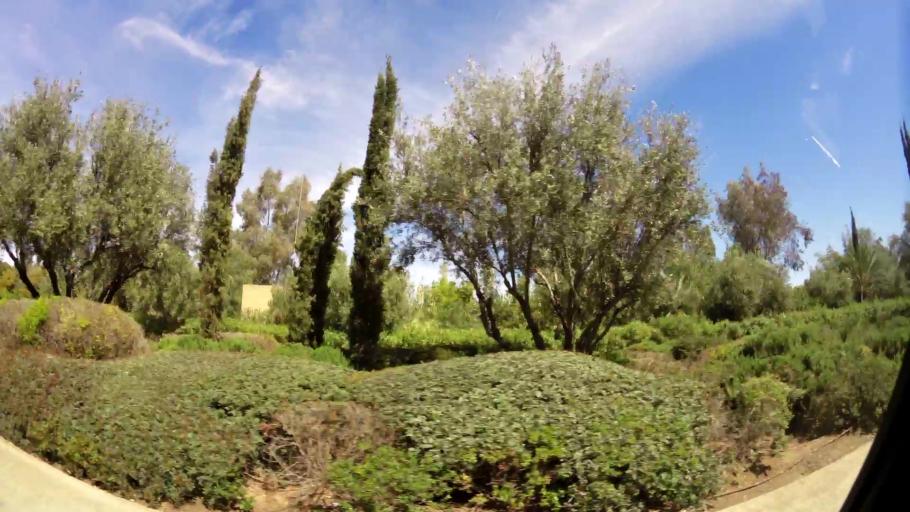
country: MA
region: Marrakech-Tensift-Al Haouz
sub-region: Marrakech
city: Marrakesh
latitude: 31.6062
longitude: -7.9547
